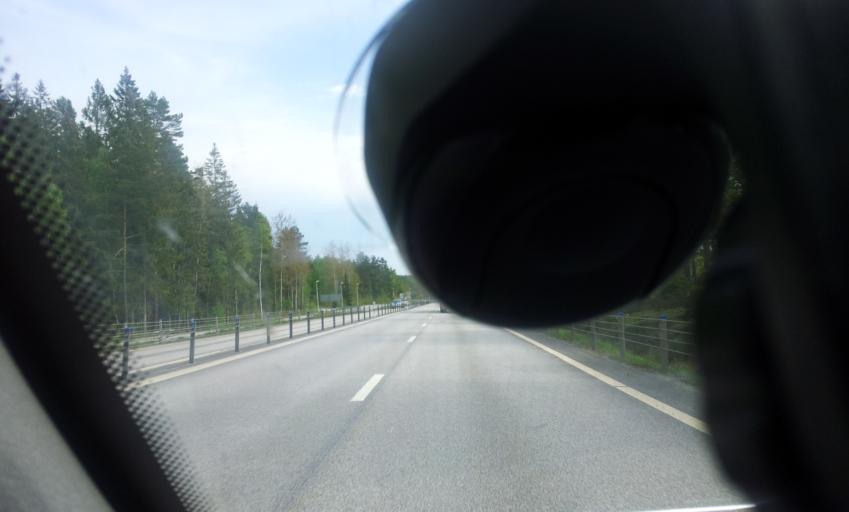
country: SE
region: Kalmar
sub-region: Vasterviks Kommun
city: Gamleby
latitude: 57.8138
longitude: 16.4857
